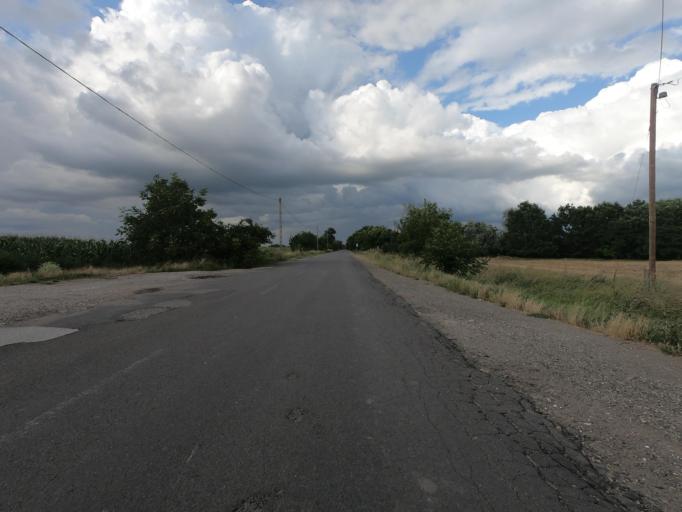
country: HU
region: Heves
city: Poroszlo
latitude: 47.6582
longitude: 20.6570
